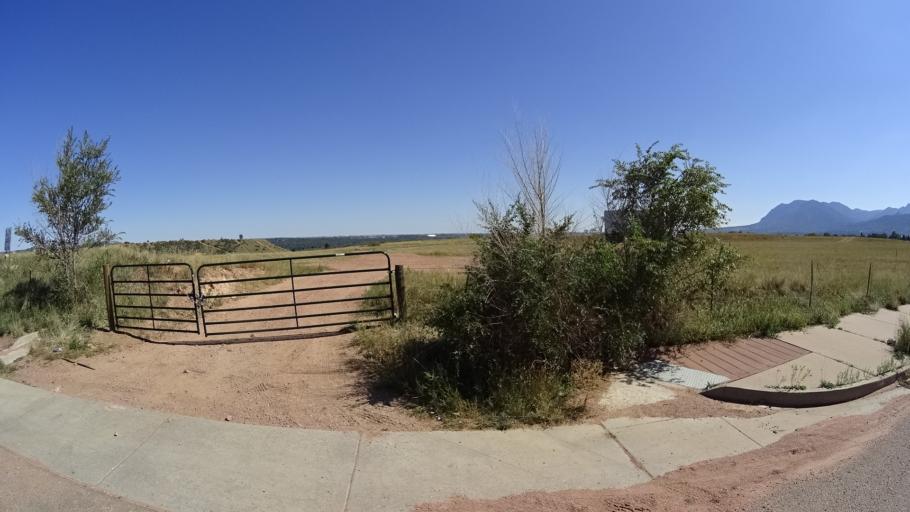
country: US
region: Colorado
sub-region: El Paso County
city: Colorado Springs
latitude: 38.8724
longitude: -104.8520
